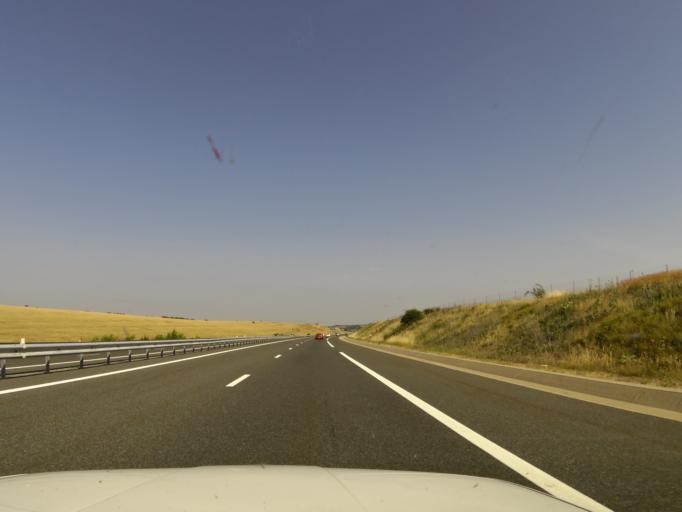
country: FR
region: Midi-Pyrenees
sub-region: Departement de l'Aveyron
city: La Cavalerie
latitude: 44.0254
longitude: 3.1156
